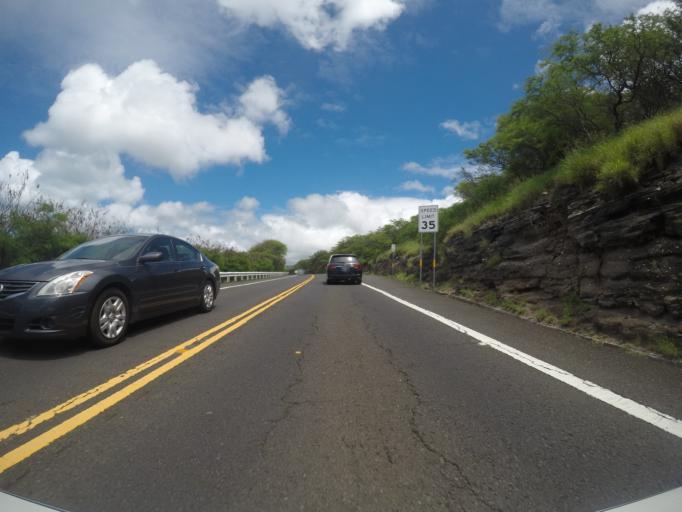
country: US
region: Hawaii
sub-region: Honolulu County
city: Waimanalo Beach
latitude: 21.2741
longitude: -157.6906
